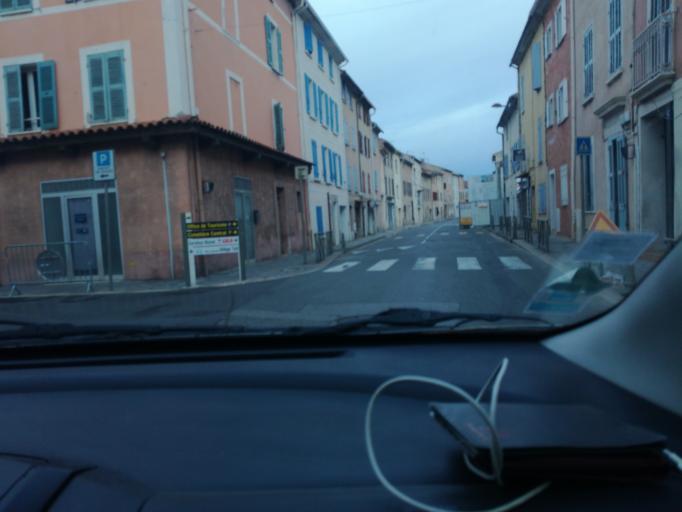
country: FR
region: Provence-Alpes-Cote d'Azur
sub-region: Departement du Var
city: La Crau
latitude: 43.1498
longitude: 6.0739
